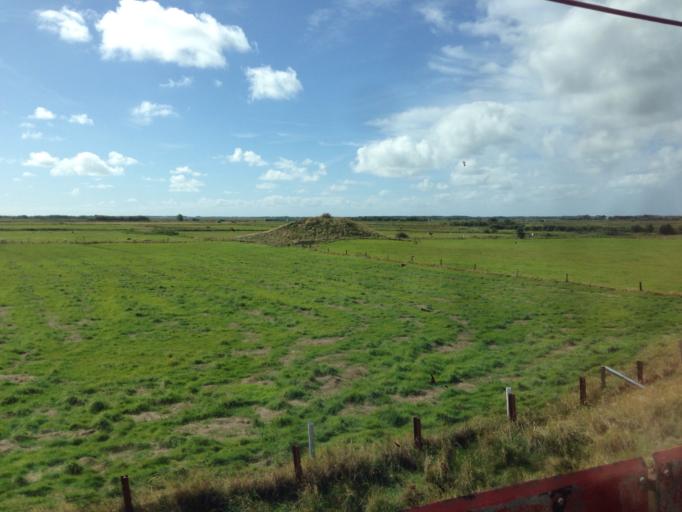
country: DE
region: Schleswig-Holstein
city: Keitum
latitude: 54.8935
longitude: 8.3564
